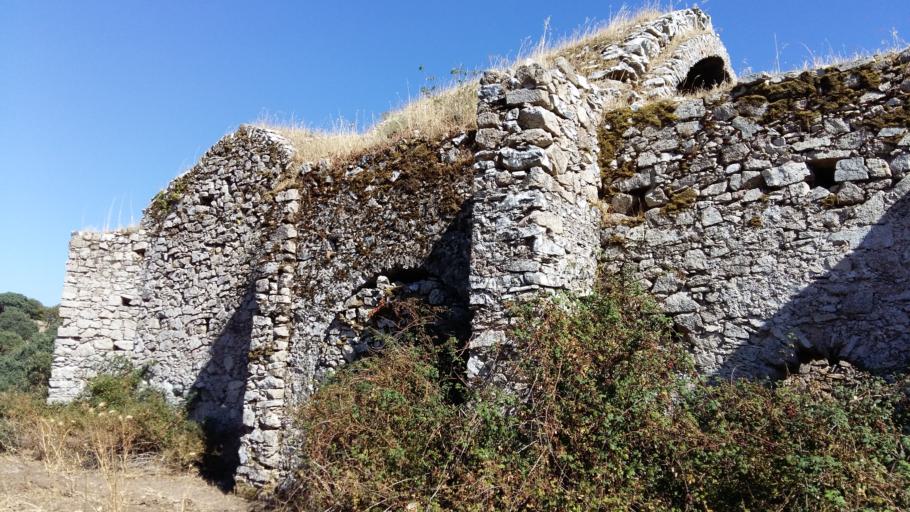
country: IT
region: Sardinia
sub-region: Provincia di Nuoro
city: Orani
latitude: 40.2563
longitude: 9.2162
